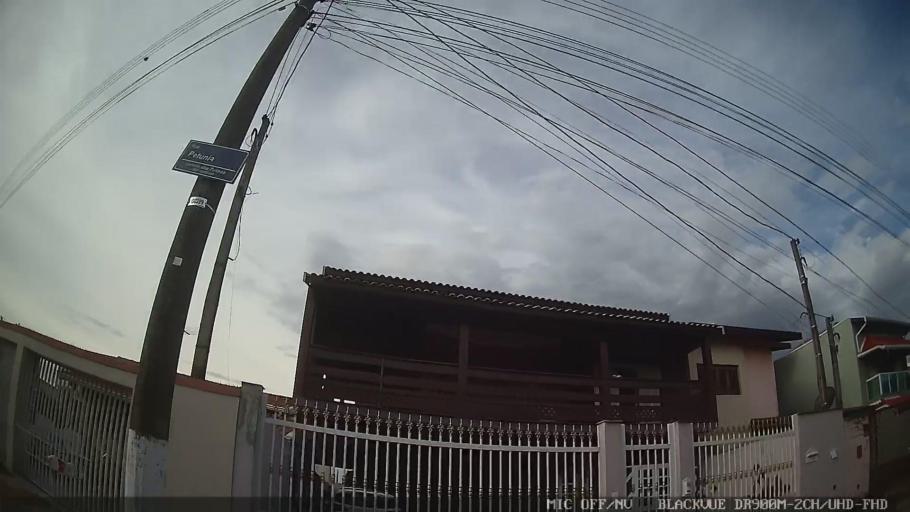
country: BR
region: Sao Paulo
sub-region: Jaguariuna
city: Jaguariuna
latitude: -22.6462
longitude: -47.0511
